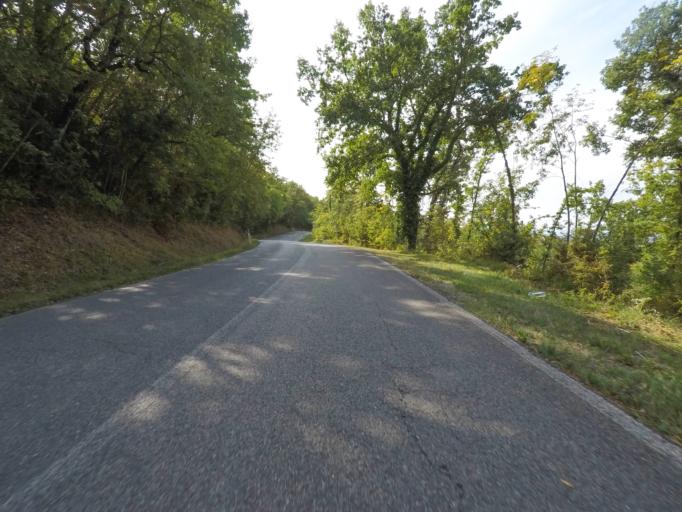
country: IT
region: Tuscany
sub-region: Provincia di Siena
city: Belverde
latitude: 43.3860
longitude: 11.3447
